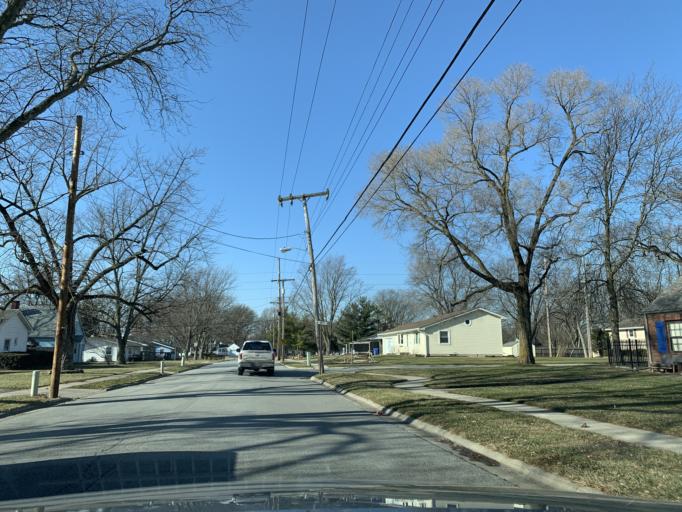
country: US
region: Indiana
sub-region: Lake County
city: Crown Point
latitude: 41.4204
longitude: -87.3735
